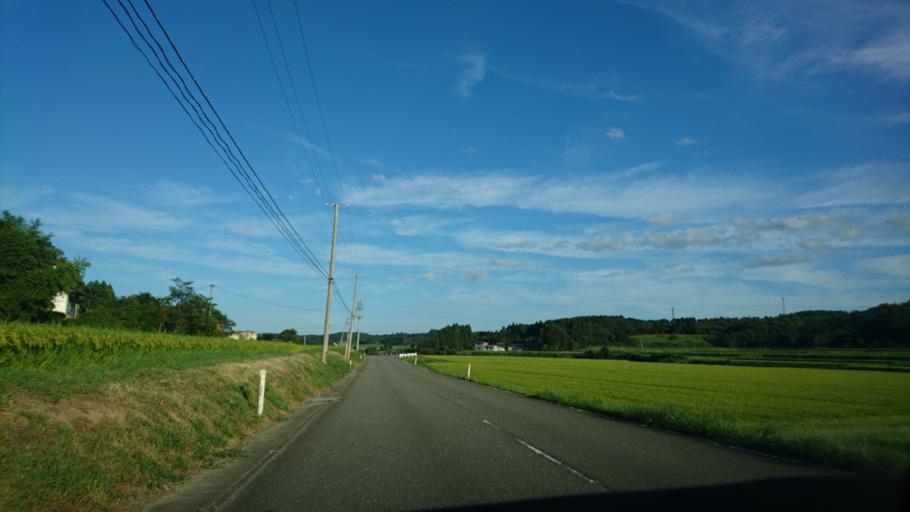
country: JP
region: Iwate
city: Ichinoseki
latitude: 38.8451
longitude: 141.1206
